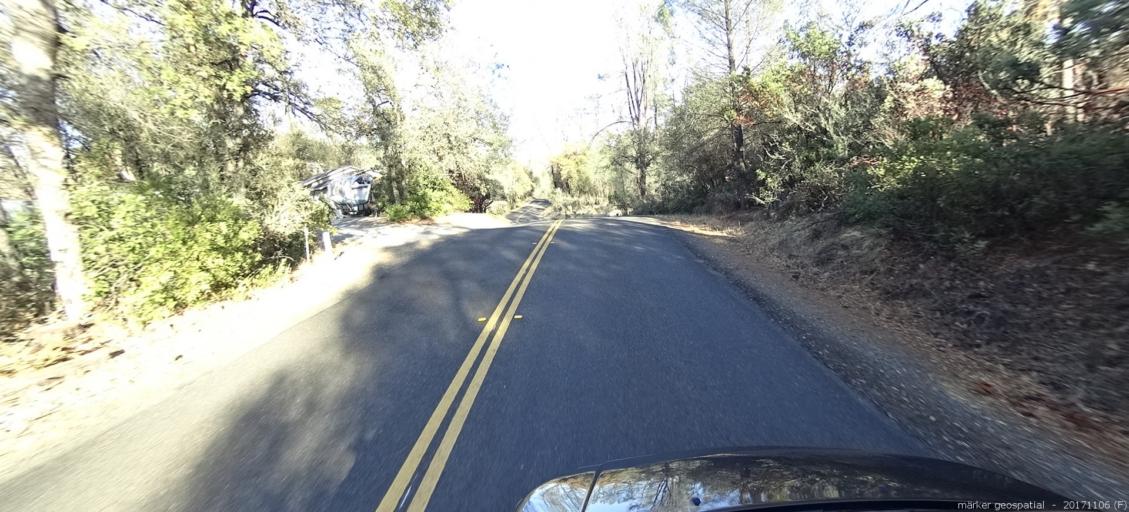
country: US
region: California
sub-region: Shasta County
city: Shasta
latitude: 40.5712
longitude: -122.4656
